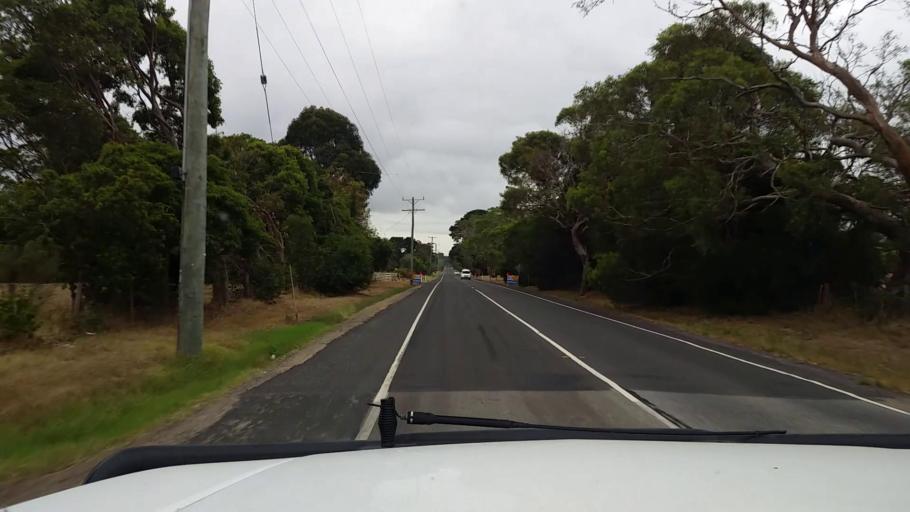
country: AU
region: Victoria
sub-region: Mornington Peninsula
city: Tyabb
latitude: -38.2580
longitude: 145.1457
